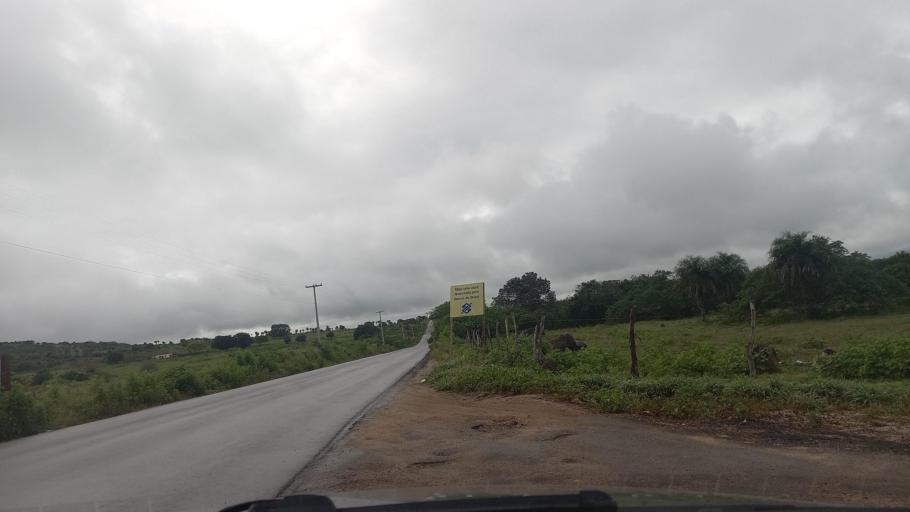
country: BR
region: Alagoas
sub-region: Sao Jose Da Tapera
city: Sao Jose da Tapera
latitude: -9.5506
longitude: -37.3111
